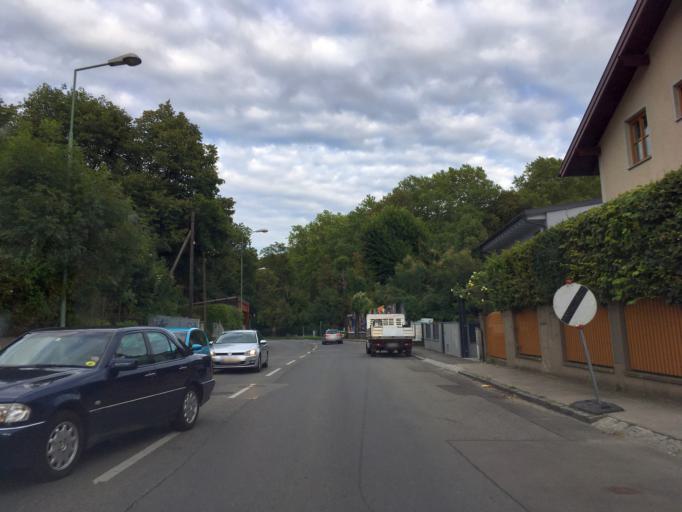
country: AT
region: Lower Austria
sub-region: Politischer Bezirk Wien-Umgebung
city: Klosterneuburg
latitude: 48.3054
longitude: 16.2926
